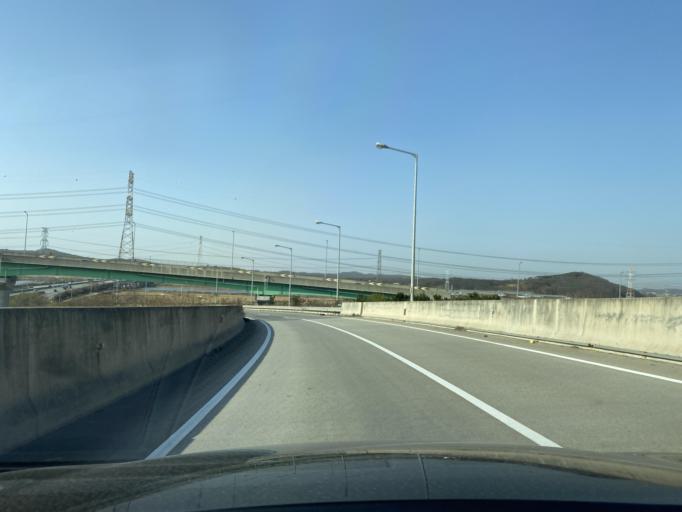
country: KR
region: Gyeonggi-do
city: Hwaseong-si
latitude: 37.0555
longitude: 126.8886
